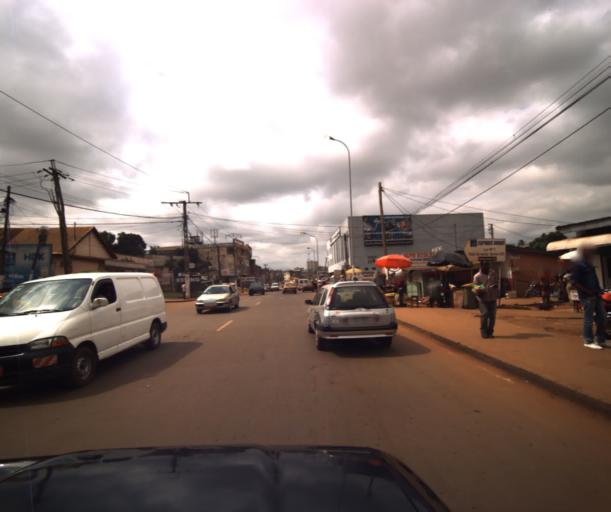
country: CM
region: Centre
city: Yaounde
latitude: 3.8569
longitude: 11.5220
